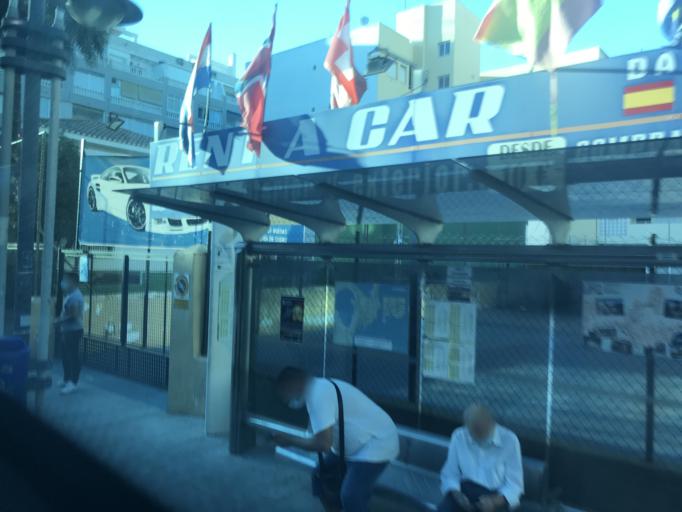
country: ES
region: Valencia
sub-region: Provincia de Alicante
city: Torrevieja
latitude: 37.9806
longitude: -0.6665
